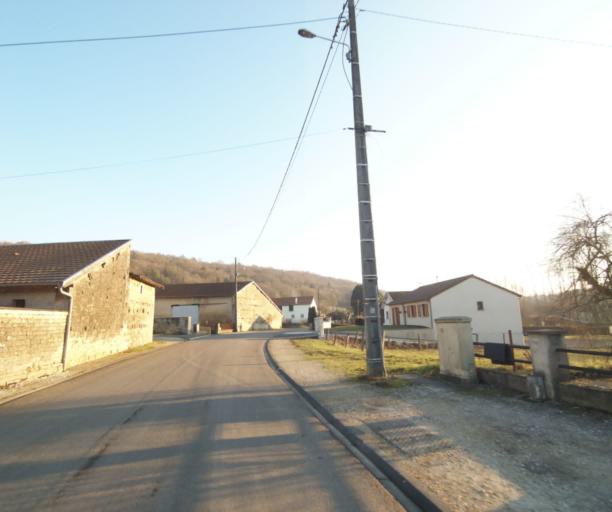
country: FR
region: Champagne-Ardenne
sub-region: Departement de la Haute-Marne
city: Chevillon
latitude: 48.5380
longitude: 5.1056
